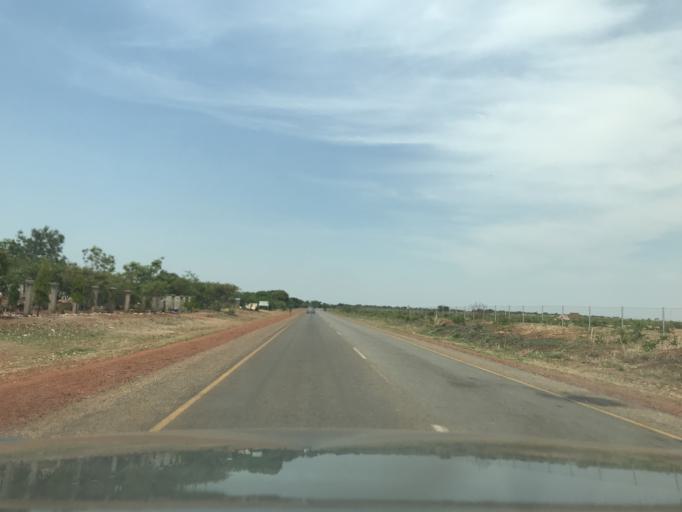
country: ZM
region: Northern
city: Kasama
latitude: -10.2191
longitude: 31.1397
